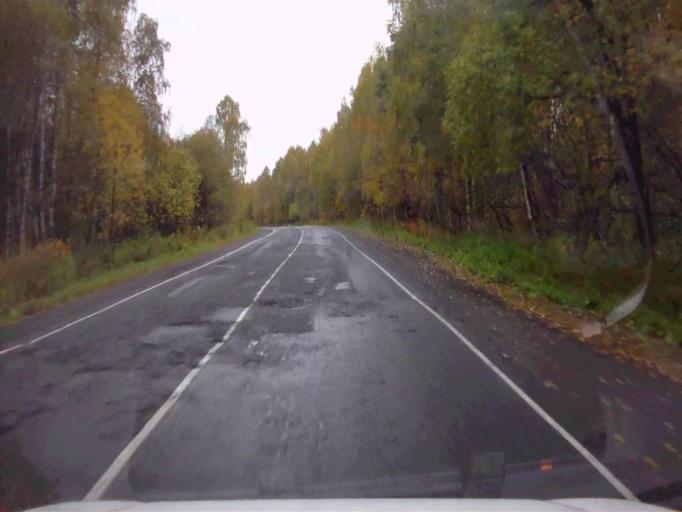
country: RU
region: Chelyabinsk
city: Nizhniy Ufaley
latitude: 56.0547
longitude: 60.0525
